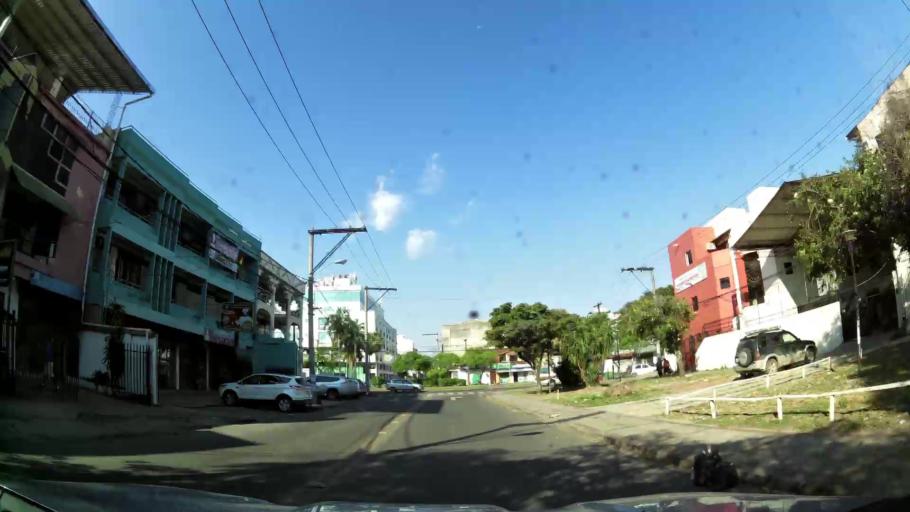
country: BO
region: Santa Cruz
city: Santa Cruz de la Sierra
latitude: -17.7832
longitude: -63.1894
